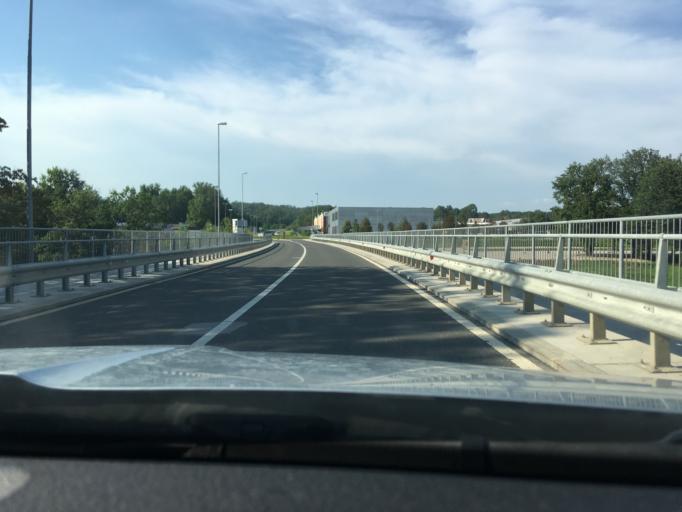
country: SI
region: Crnomelj
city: Crnomelj
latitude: 45.5705
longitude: 15.1810
